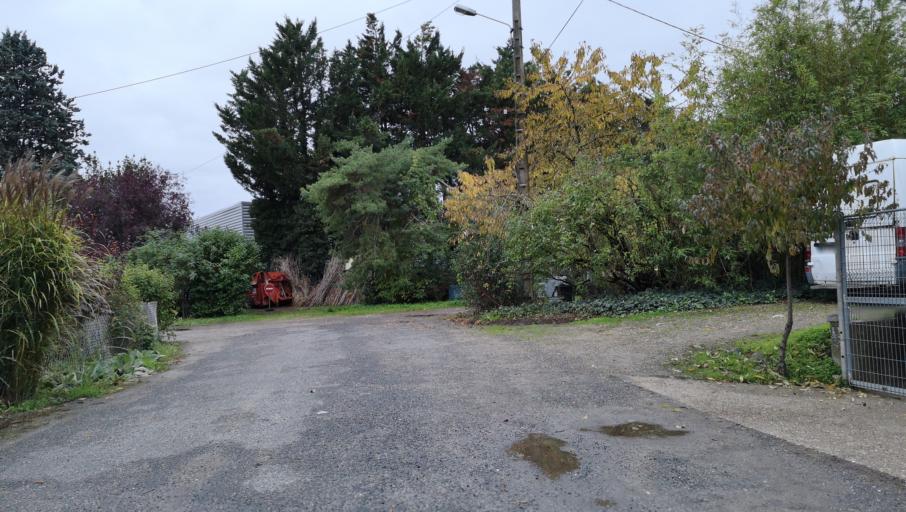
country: FR
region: Centre
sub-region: Departement du Loiret
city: Semoy
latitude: 47.9178
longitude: 1.9564
